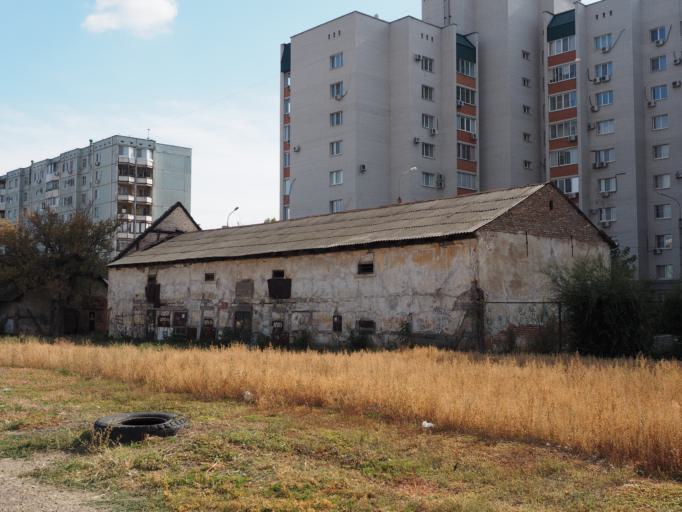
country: RU
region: Volgograd
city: Krasnoslobodsk
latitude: 48.5096
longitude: 44.5461
